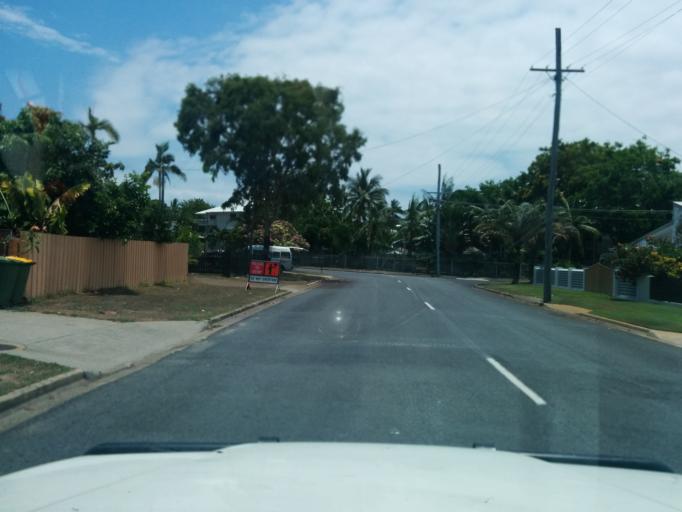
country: AU
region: Queensland
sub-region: Cairns
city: Yorkeys Knob
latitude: -16.8376
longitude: 145.7389
